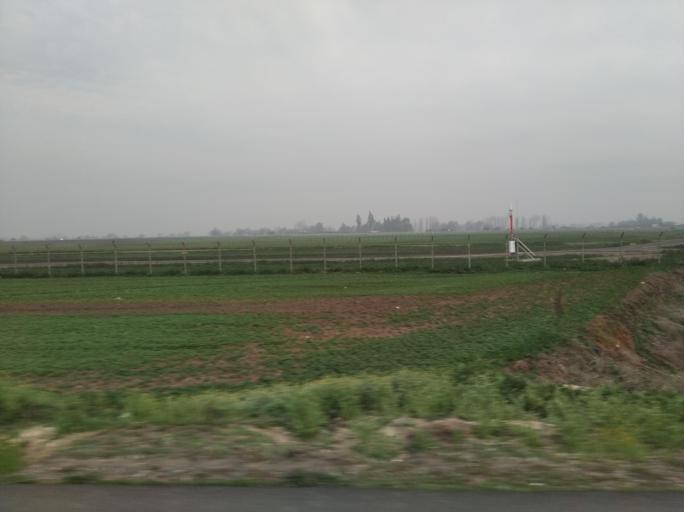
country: CL
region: Santiago Metropolitan
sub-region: Provincia de Santiago
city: Lo Prado
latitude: -33.3683
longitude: -70.7994
